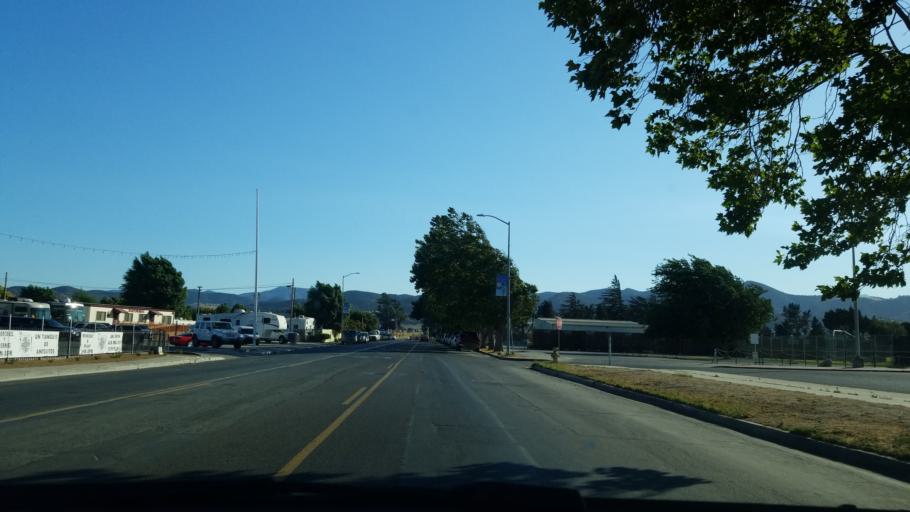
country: US
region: California
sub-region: Monterey County
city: King City
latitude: 36.2079
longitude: -121.1343
